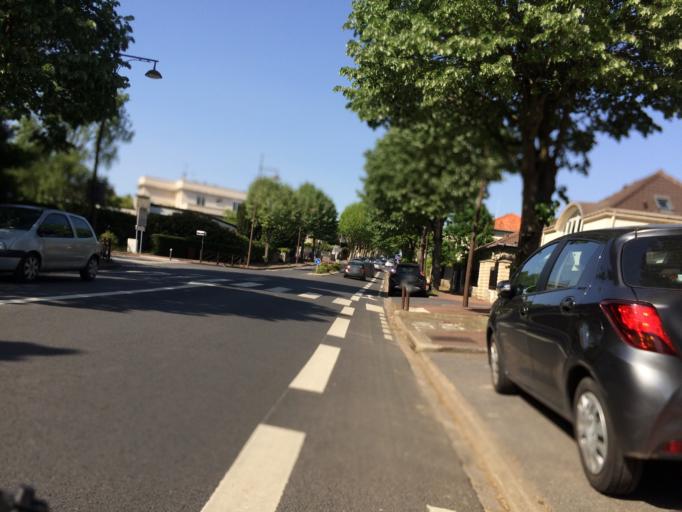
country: FR
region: Ile-de-France
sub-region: Departement des Hauts-de-Seine
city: Sceaux
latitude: 48.7754
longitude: 2.2777
